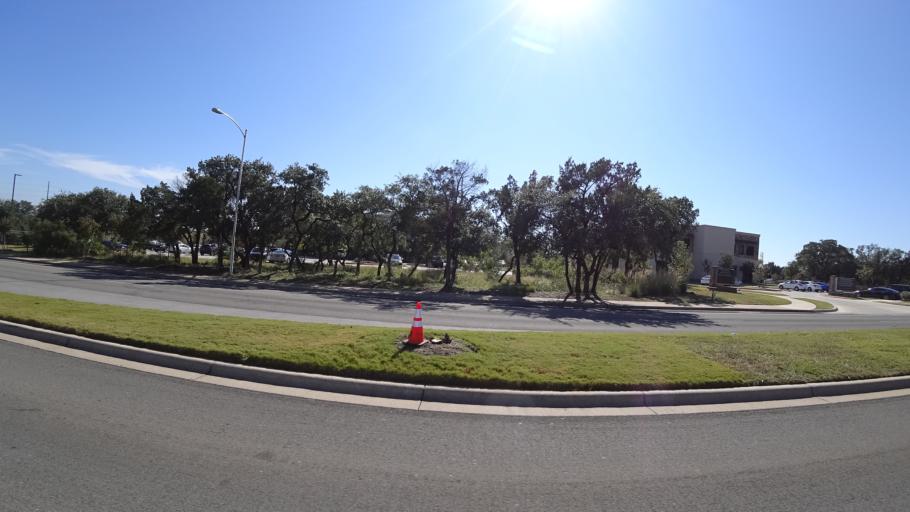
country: US
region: Texas
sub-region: Travis County
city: Shady Hollow
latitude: 30.2087
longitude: -97.8628
